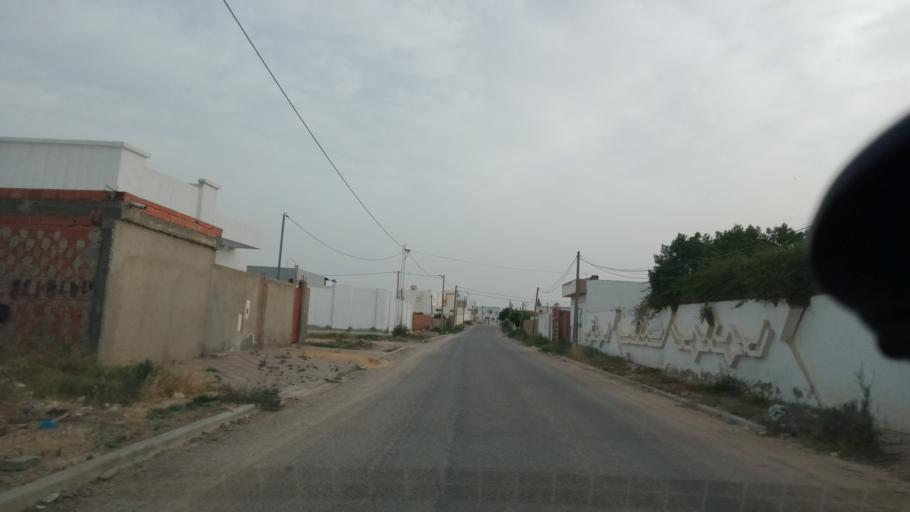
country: TN
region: Safaqis
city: Al Qarmadah
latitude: 34.7868
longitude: 10.7702
